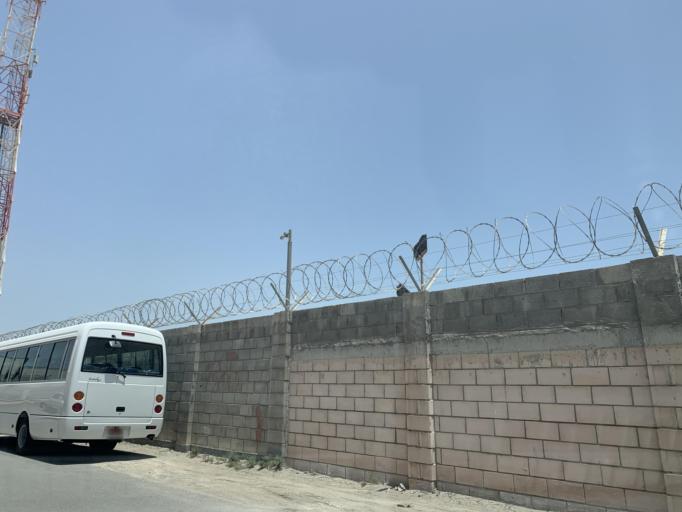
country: BH
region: Northern
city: Sitrah
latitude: 26.1659
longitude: 50.6092
